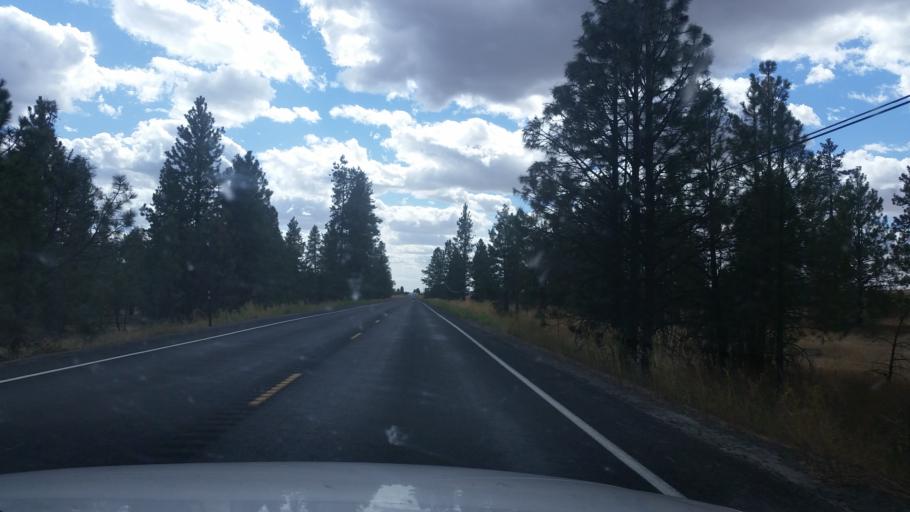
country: US
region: Washington
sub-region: Spokane County
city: Medical Lake
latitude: 47.5409
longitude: -117.7070
